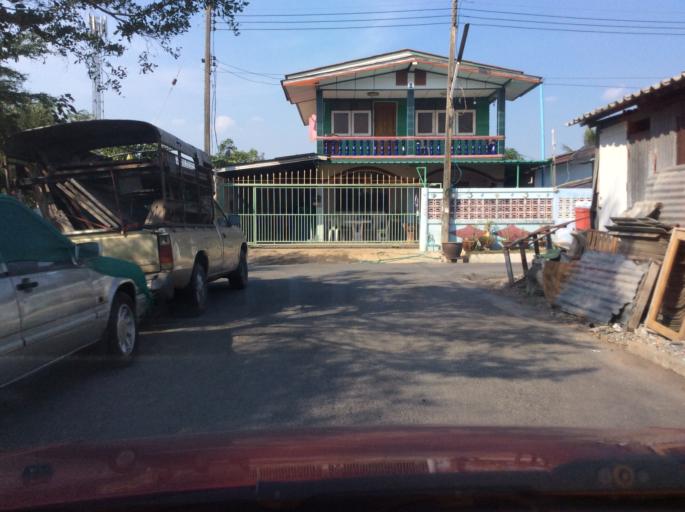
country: TH
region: Pathum Thani
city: Lam Luk Ka
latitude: 13.9483
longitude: 100.7281
